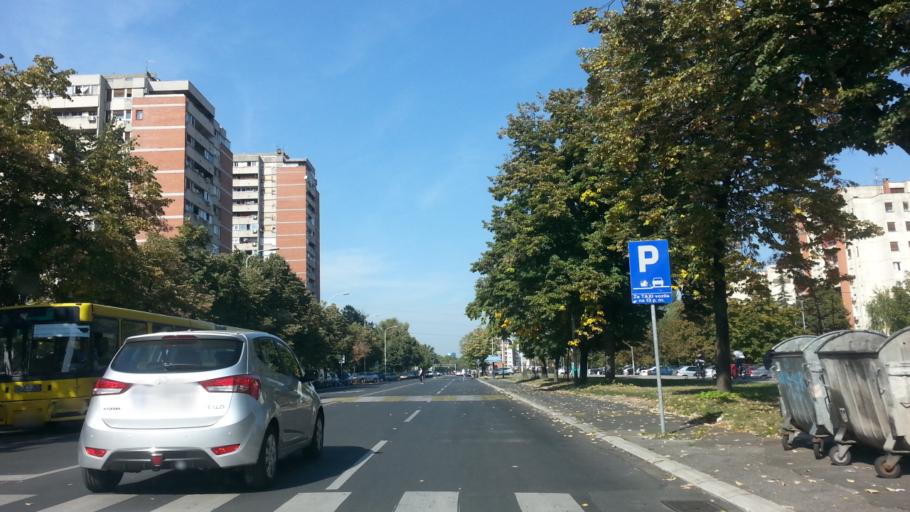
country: RS
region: Central Serbia
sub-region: Belgrade
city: Novi Beograd
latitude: 44.8009
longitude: 20.3999
